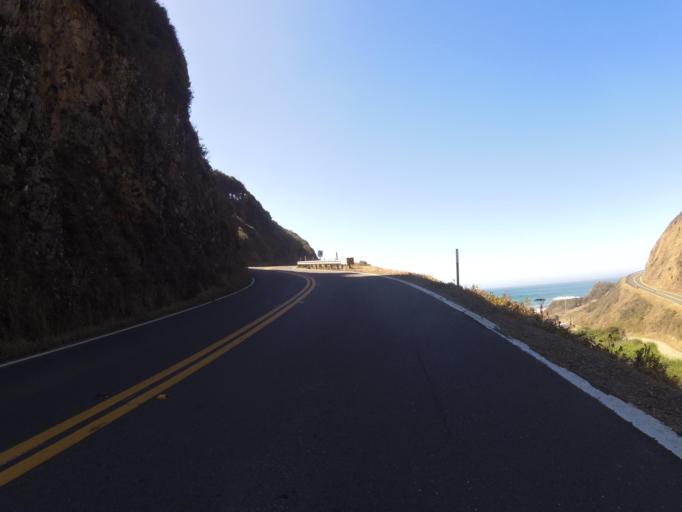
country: US
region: California
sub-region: Mendocino County
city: Fort Bragg
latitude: 39.6126
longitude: -123.7796
